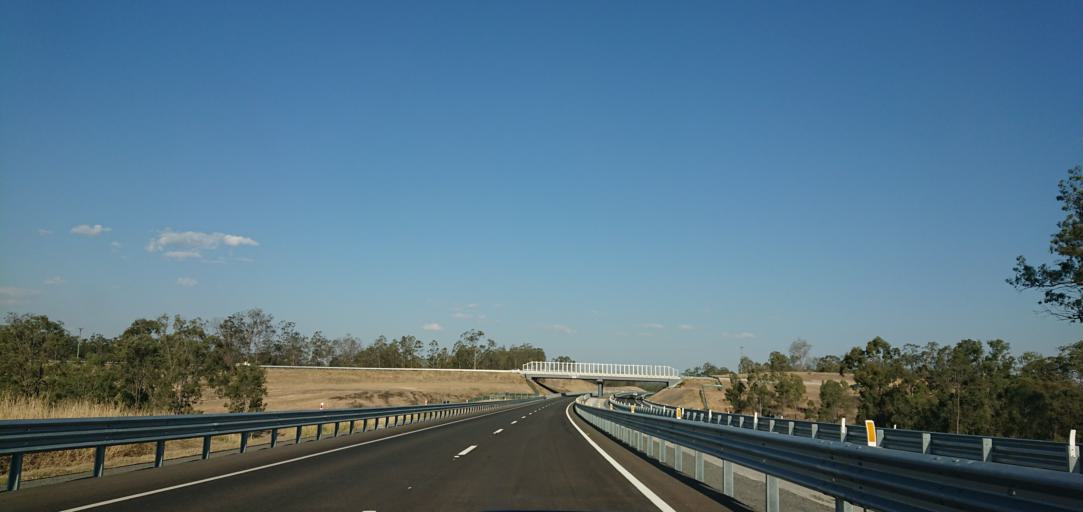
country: AU
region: Queensland
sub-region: Toowoomba
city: East Toowoomba
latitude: -27.5231
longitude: 152.0631
